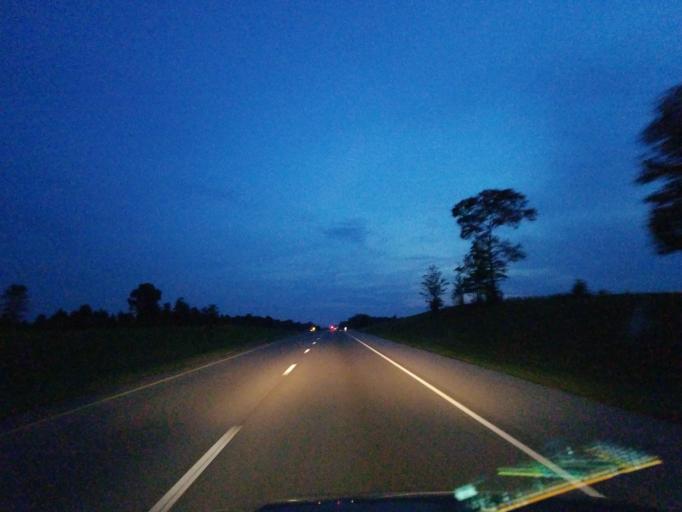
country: US
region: Mississippi
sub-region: Jones County
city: Ellisville
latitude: 31.5530
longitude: -89.2628
